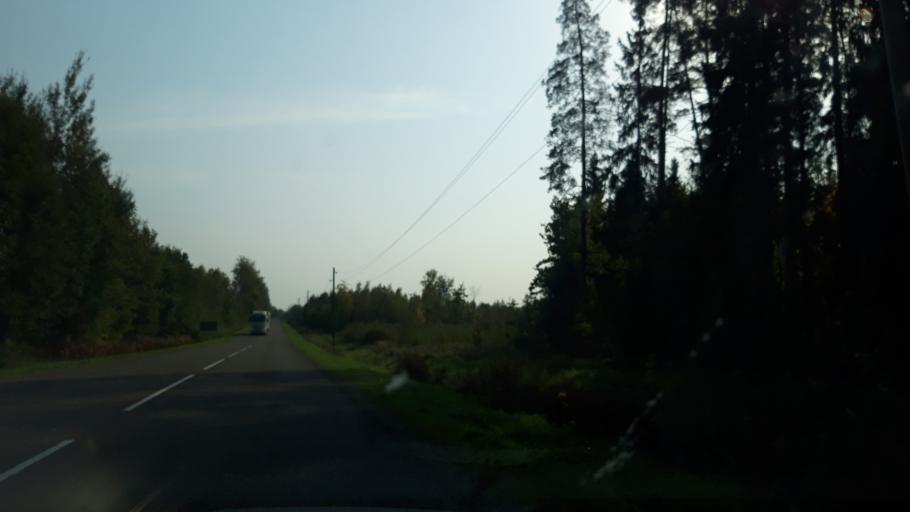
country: LV
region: Burtnieki
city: Matisi
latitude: 57.6362
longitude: 25.2556
